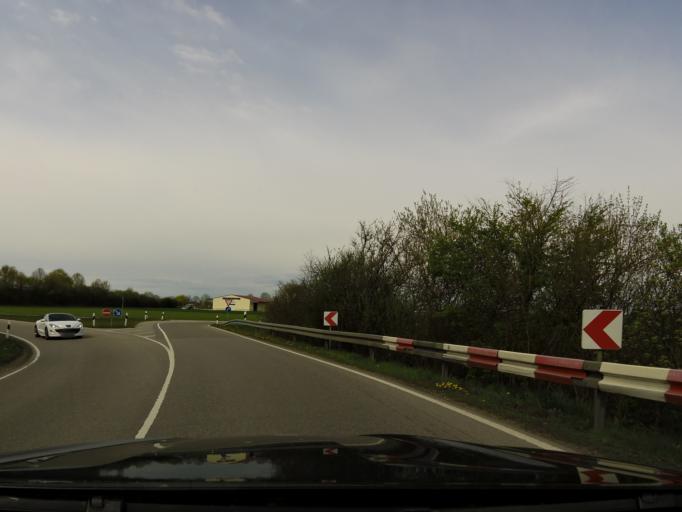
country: DE
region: Bavaria
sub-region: Upper Bavaria
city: Erding
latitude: 48.3211
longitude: 11.8841
